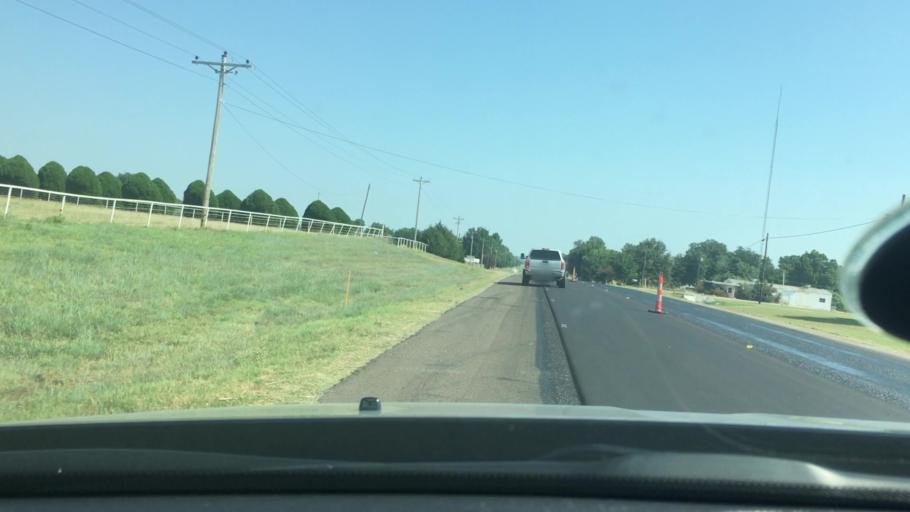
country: US
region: Oklahoma
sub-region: Garvin County
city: Lindsay
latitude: 34.8028
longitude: -97.5983
